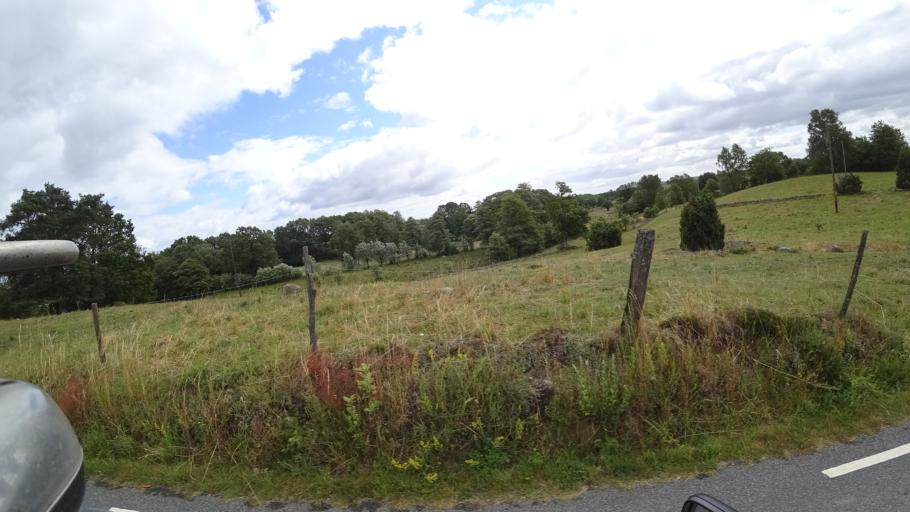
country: SE
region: Skane
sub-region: Kristianstads Kommun
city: Degeberga
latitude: 55.7293
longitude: 14.0003
